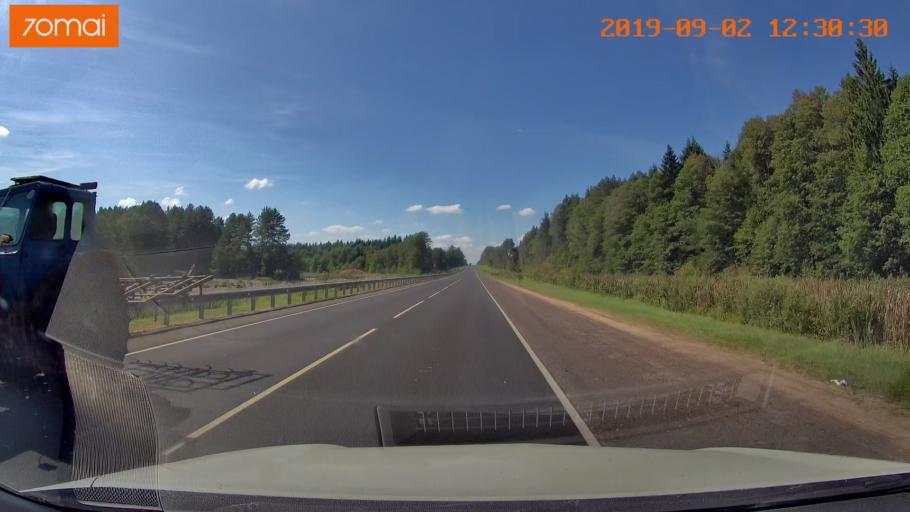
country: RU
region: Smolensk
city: Shumyachi
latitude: 53.8316
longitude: 32.4730
